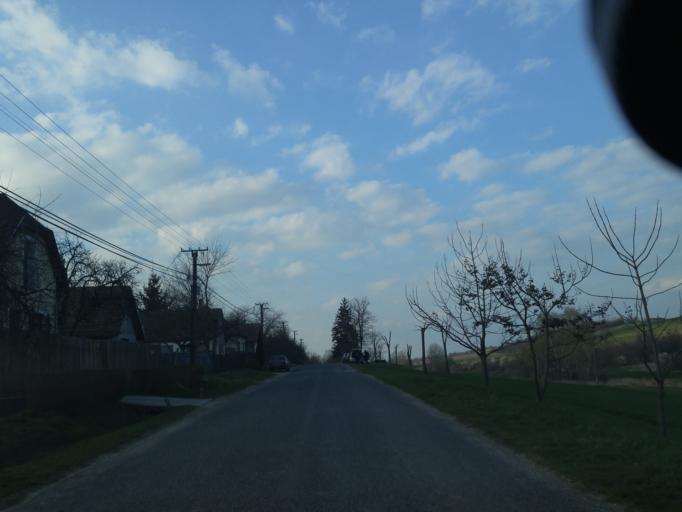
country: HU
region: Somogy
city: Adand
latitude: 46.8085
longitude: 18.1087
